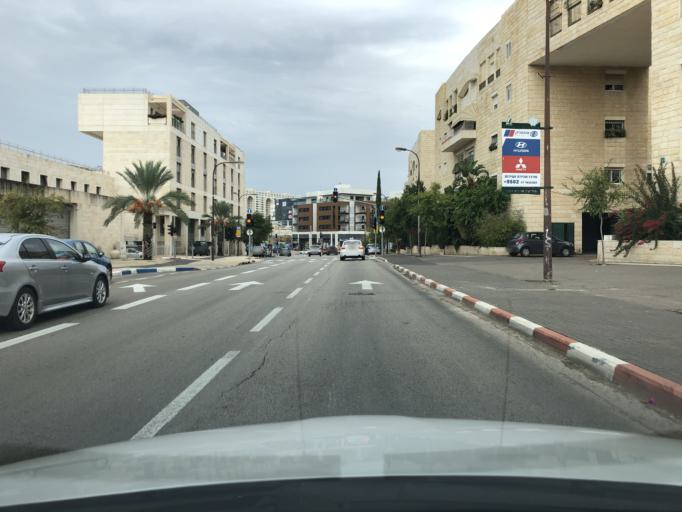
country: IL
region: Central District
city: Modiin
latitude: 31.8994
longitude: 35.0096
